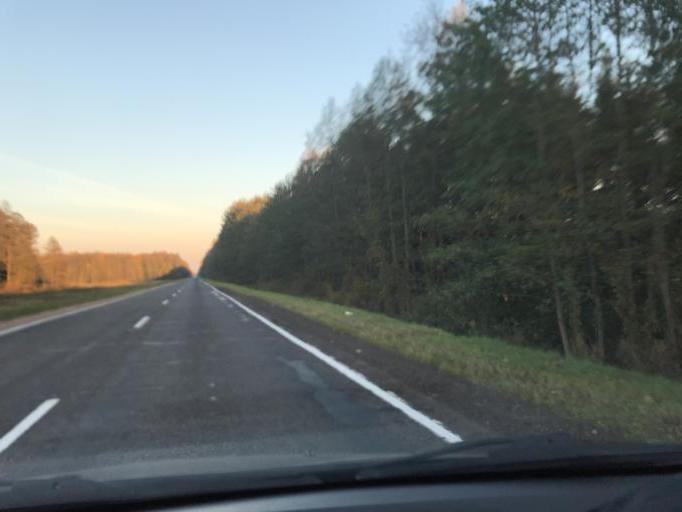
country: BY
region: Mogilev
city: Hlusk
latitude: 53.0692
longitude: 28.5842
